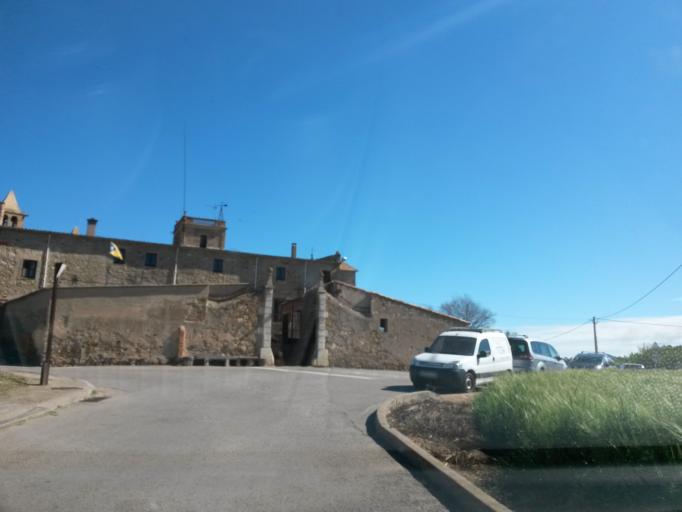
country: ES
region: Catalonia
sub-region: Provincia de Girona
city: Madremanya
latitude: 41.9887
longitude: 2.9568
